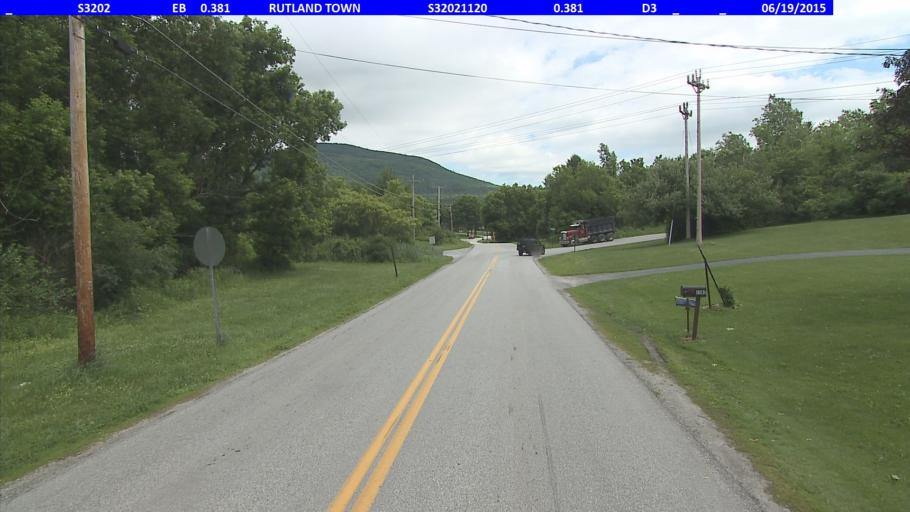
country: US
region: Vermont
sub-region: Rutland County
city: Rutland
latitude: 43.5888
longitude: -72.9616
